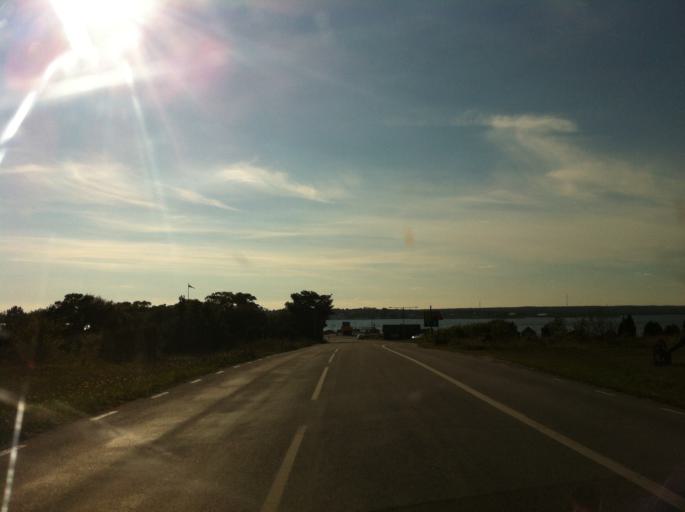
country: SE
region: Gotland
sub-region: Gotland
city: Slite
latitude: 57.8695
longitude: 19.0844
